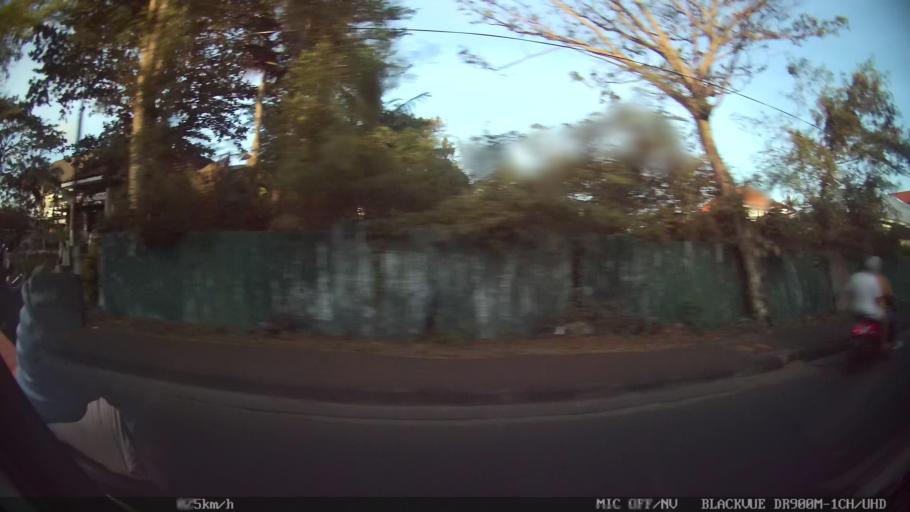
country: ID
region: Bali
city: Bualu
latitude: -8.7784
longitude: 115.2239
